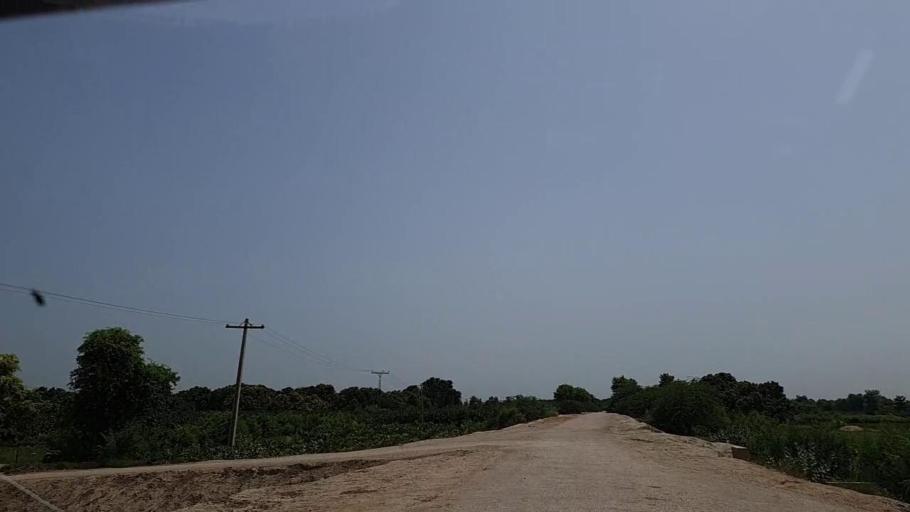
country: PK
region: Sindh
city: Kandiaro
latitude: 27.0437
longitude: 68.1306
